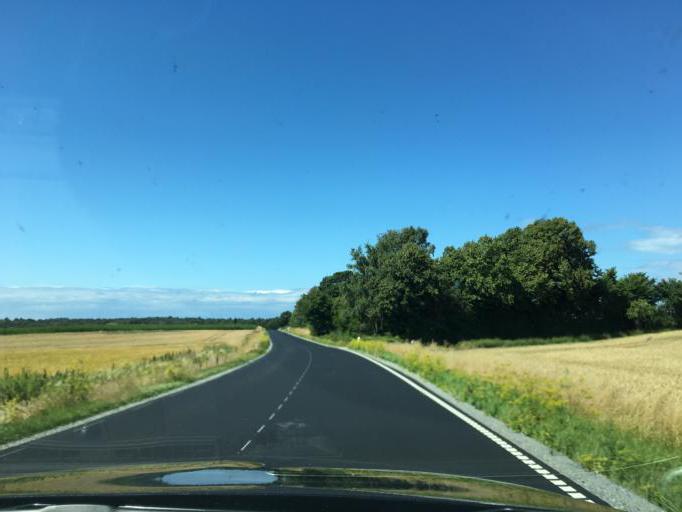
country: DK
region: Capital Region
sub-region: Gribskov Kommune
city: Helsinge
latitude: 56.0826
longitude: 12.1840
